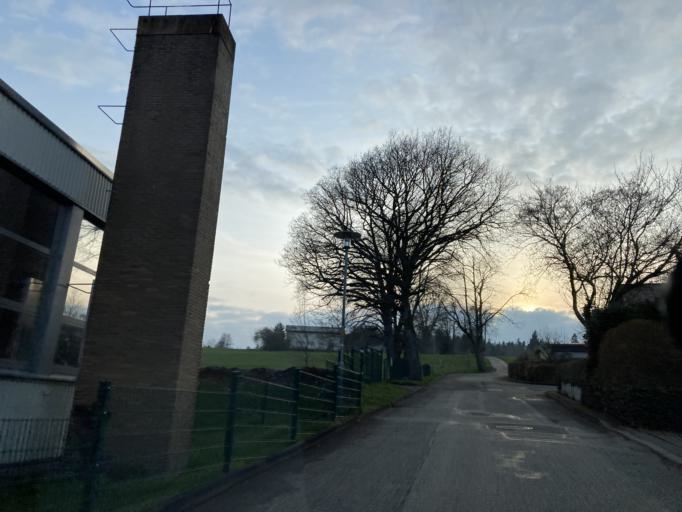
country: DE
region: Baden-Wuerttemberg
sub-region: Karlsruhe Region
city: Schomberg
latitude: 48.7877
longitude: 8.6389
